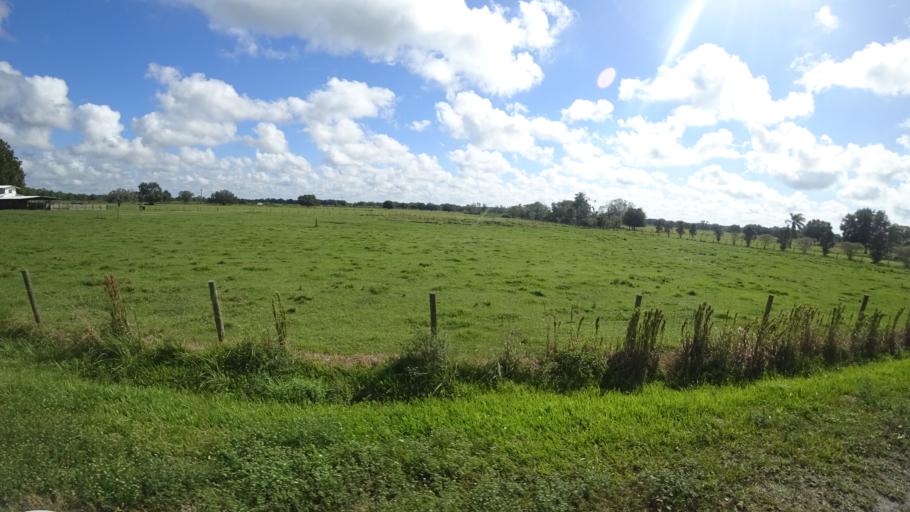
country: US
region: Florida
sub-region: Sarasota County
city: Lake Sarasota
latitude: 27.3690
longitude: -82.2193
